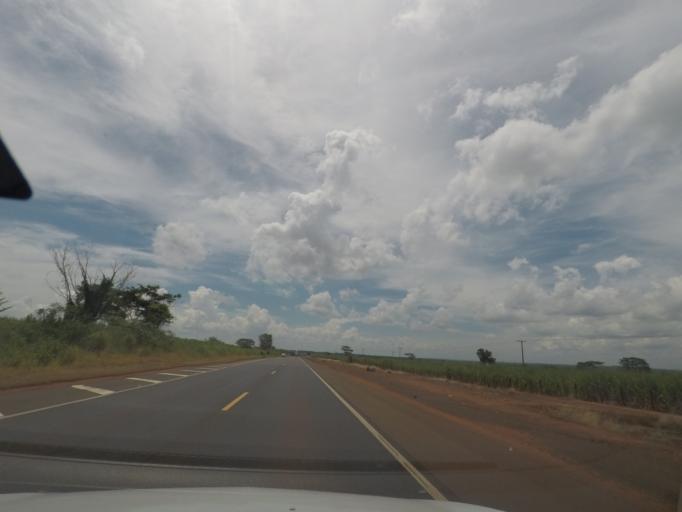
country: BR
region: Sao Paulo
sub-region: Barretos
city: Barretos
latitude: -20.3855
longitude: -48.6412
